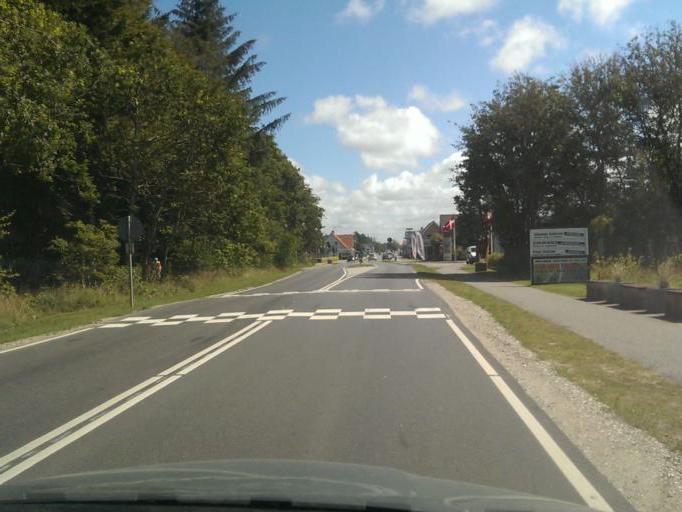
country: DK
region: North Denmark
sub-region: Jammerbugt Kommune
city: Pandrup
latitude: 57.2491
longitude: 9.6113
